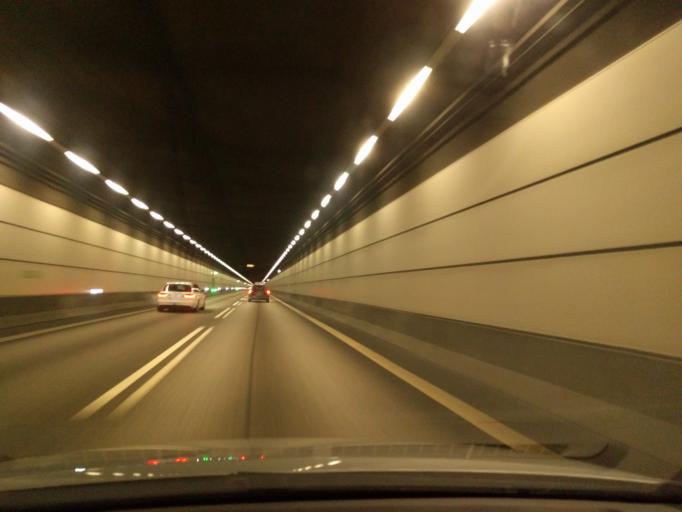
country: DK
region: Capital Region
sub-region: Dragor Kommune
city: Dragor
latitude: 55.6129
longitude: 12.7226
